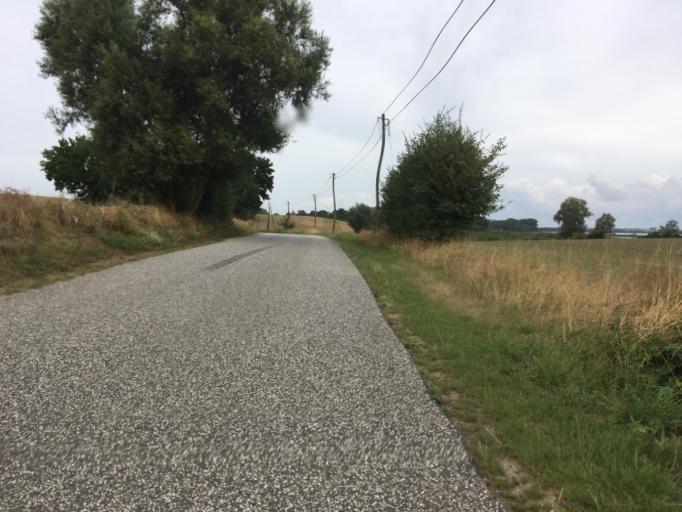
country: DE
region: Brandenburg
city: Gerswalde
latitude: 53.1736
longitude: 13.8449
